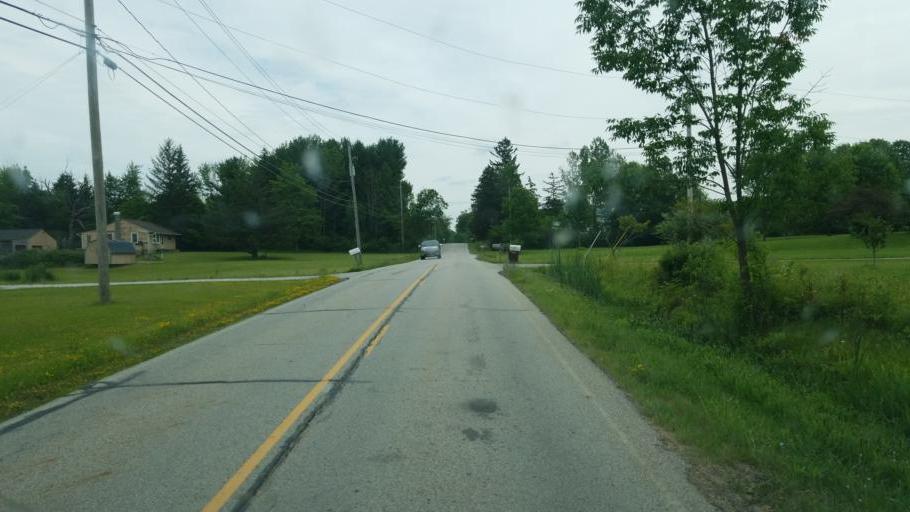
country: US
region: Ohio
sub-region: Geauga County
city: Burton
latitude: 41.4806
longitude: -81.2204
